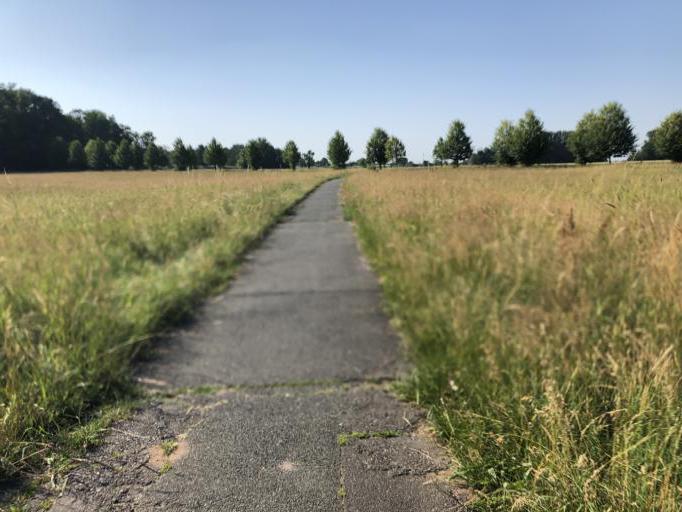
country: DE
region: Bavaria
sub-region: Regierungsbezirk Mittelfranken
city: Furth
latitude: 49.5286
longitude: 11.0080
